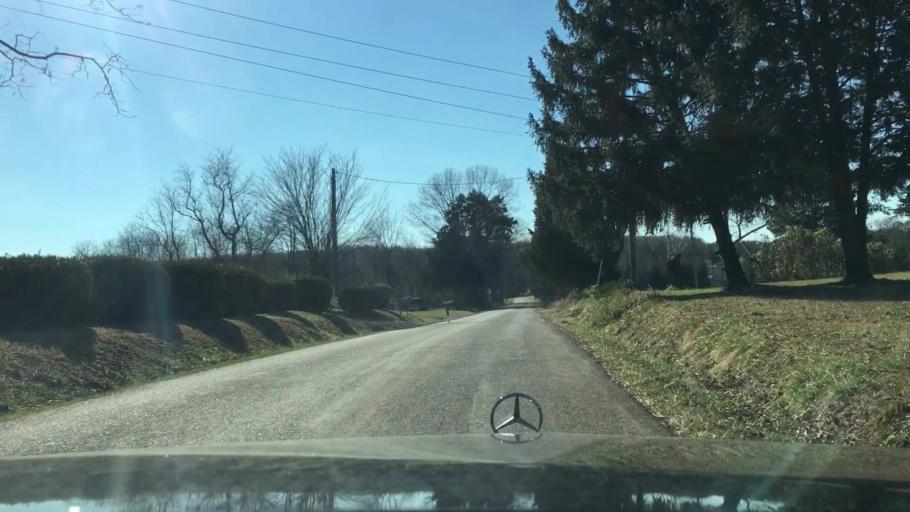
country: US
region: Virginia
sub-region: Campbell County
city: Altavista
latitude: 37.1895
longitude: -79.3137
